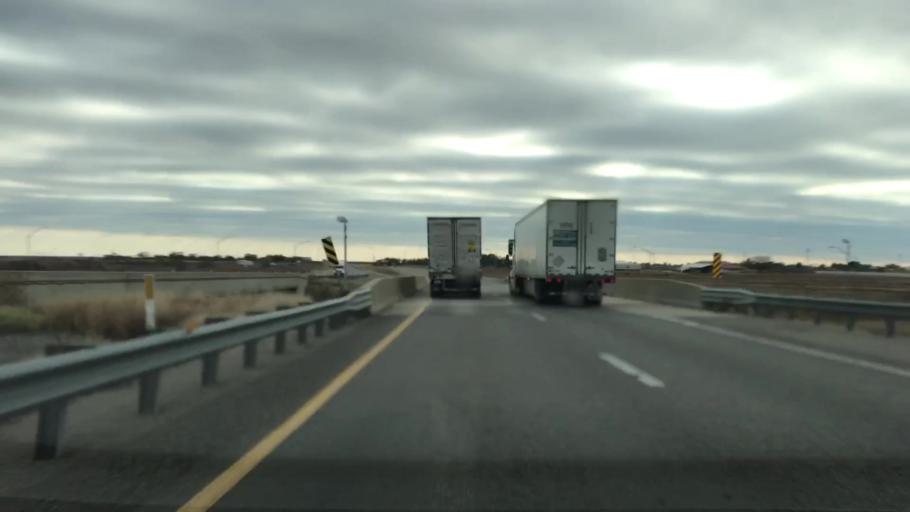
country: US
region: Oklahoma
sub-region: Beckham County
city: Sayre
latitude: 35.3160
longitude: -99.6126
